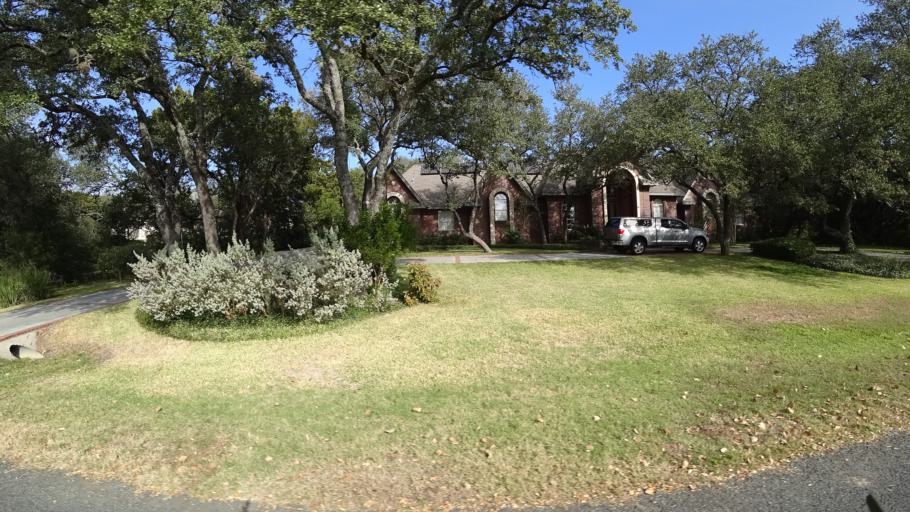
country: US
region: Texas
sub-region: Travis County
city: West Lake Hills
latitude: 30.3753
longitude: -97.8174
